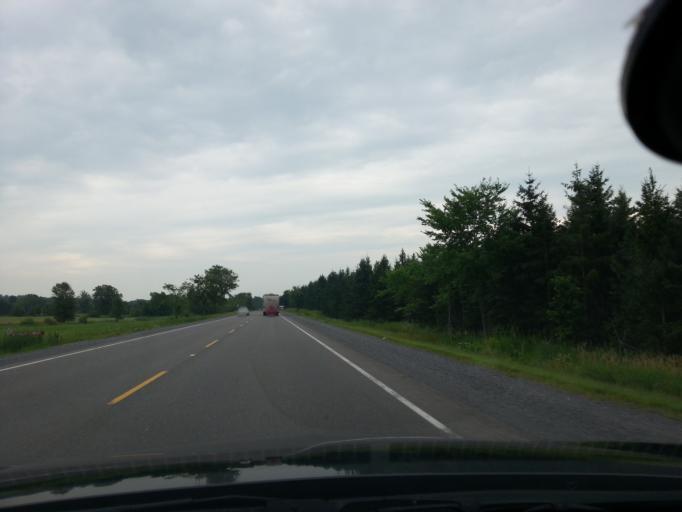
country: CA
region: Quebec
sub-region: Outaouais
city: Papineauville
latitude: 45.5614
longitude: -75.0767
